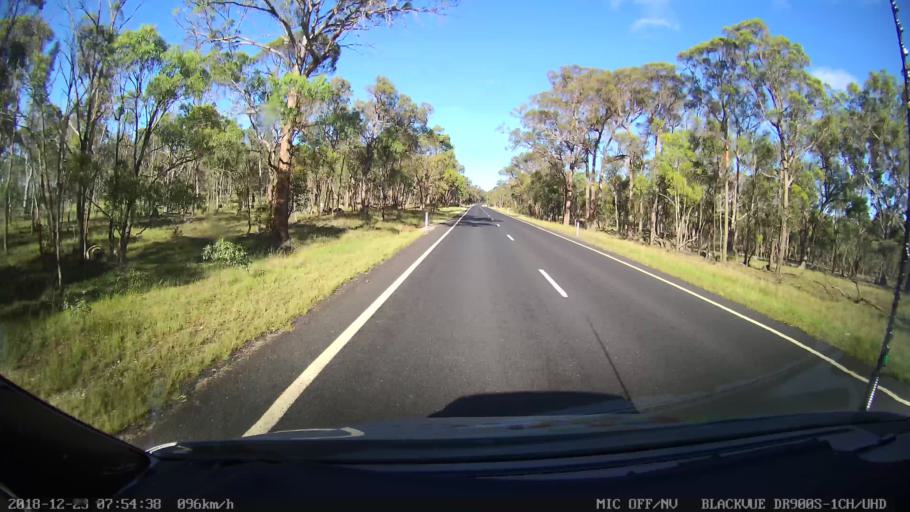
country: AU
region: New South Wales
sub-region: Armidale Dumaresq
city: Armidale
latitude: -30.5442
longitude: 151.7931
